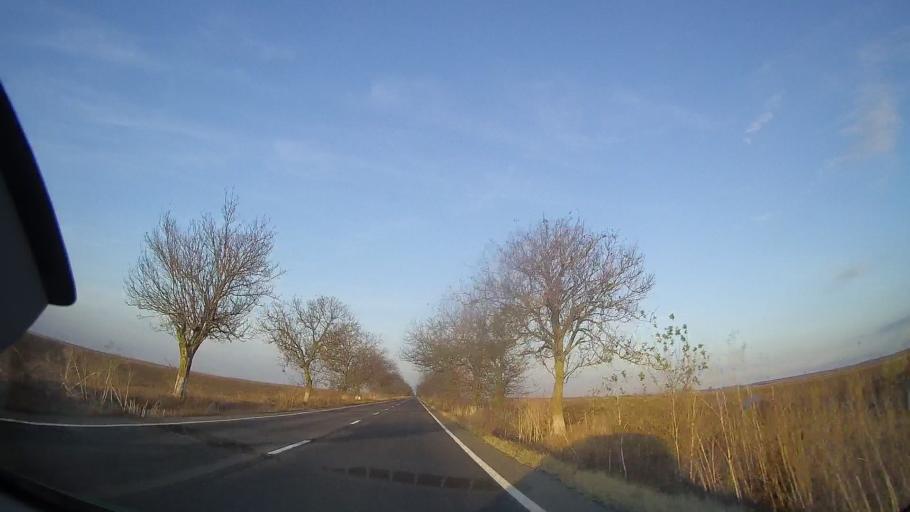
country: RO
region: Constanta
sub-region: Comuna Comana
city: Comana
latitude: 43.9164
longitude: 28.3436
